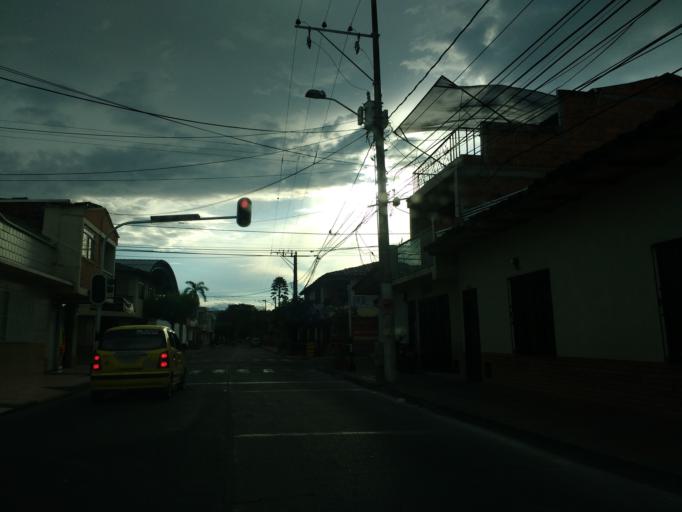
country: CO
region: Valle del Cauca
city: Cartago
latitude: 4.7478
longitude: -75.9216
